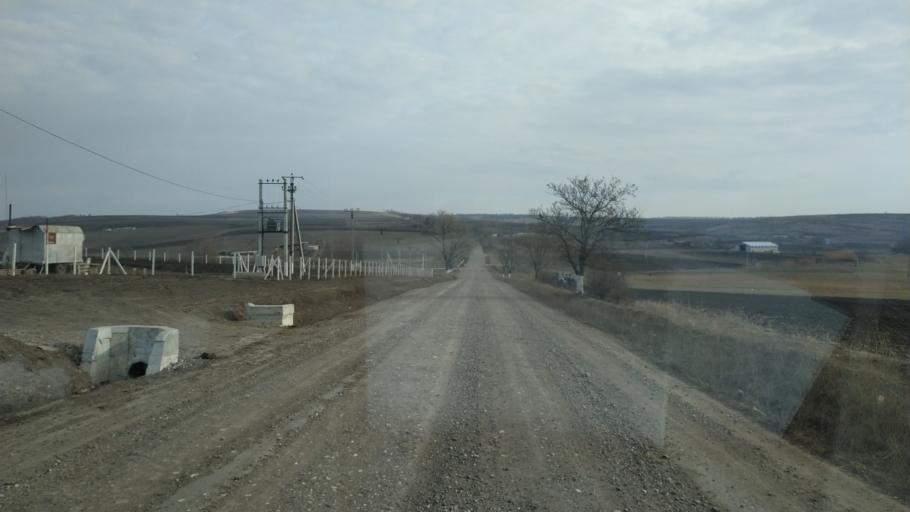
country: MD
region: Chisinau
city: Vadul lui Voda
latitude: 46.9731
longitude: 29.0724
